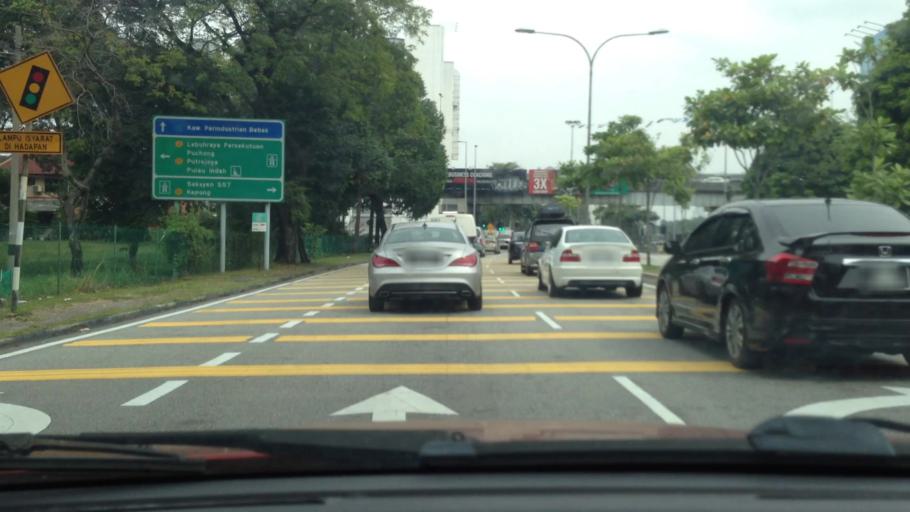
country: MY
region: Selangor
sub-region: Petaling
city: Petaling Jaya
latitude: 3.0925
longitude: 101.6072
